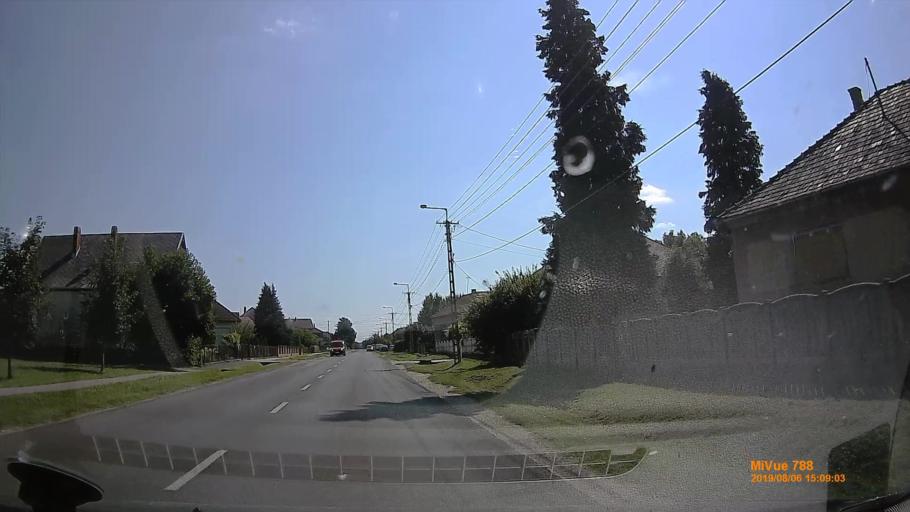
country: HU
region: Zala
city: Nagykanizsa
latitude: 46.4080
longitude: 16.9846
